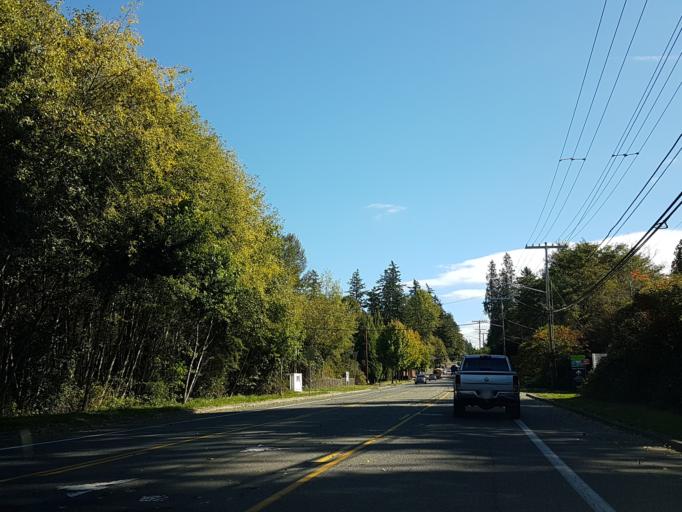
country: US
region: Washington
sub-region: King County
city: Bothell
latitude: 47.7912
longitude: -122.1956
